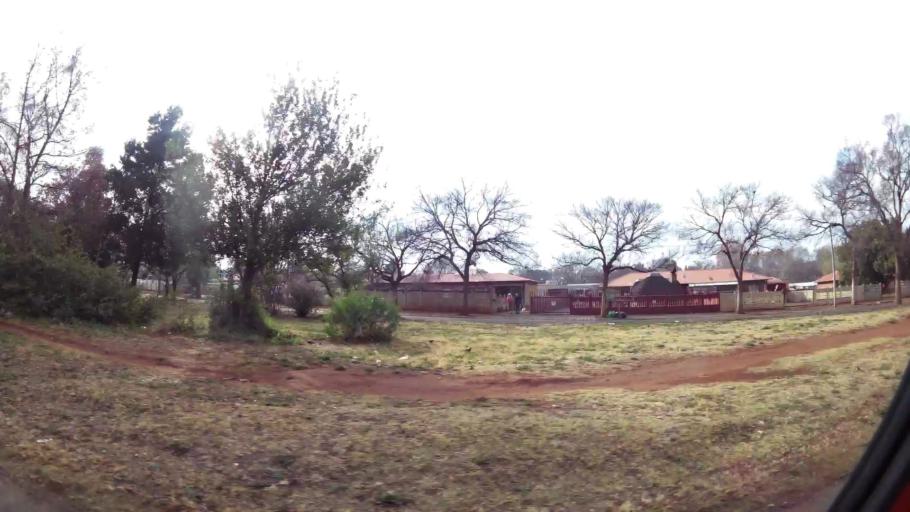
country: ZA
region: Gauteng
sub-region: Sedibeng District Municipality
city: Vanderbijlpark
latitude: -26.7002
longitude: 27.8138
